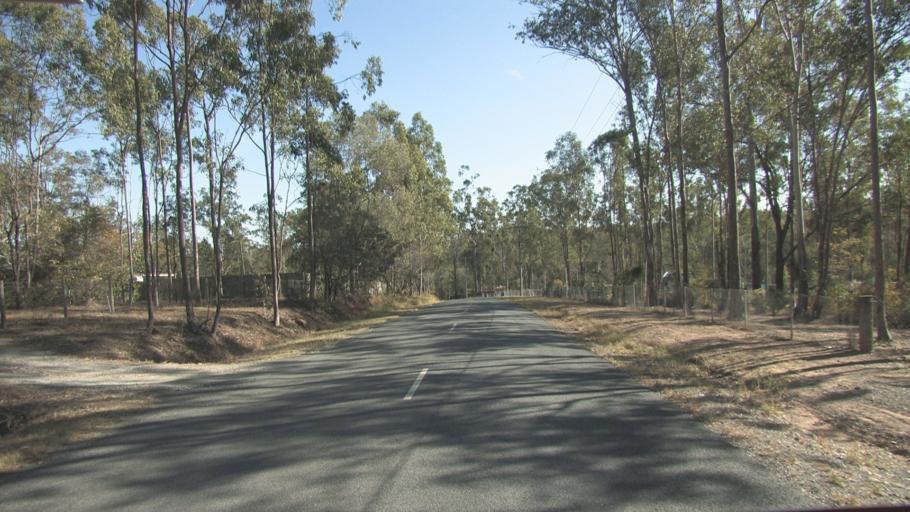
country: AU
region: Queensland
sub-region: Logan
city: Cedar Vale
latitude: -27.8424
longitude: 153.0559
